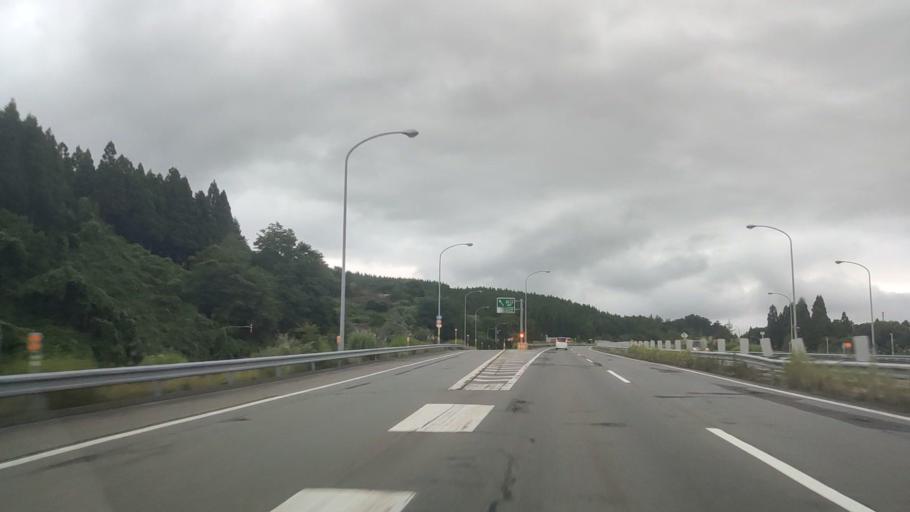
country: JP
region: Hokkaido
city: Nanae
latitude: 41.9007
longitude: 140.7026
